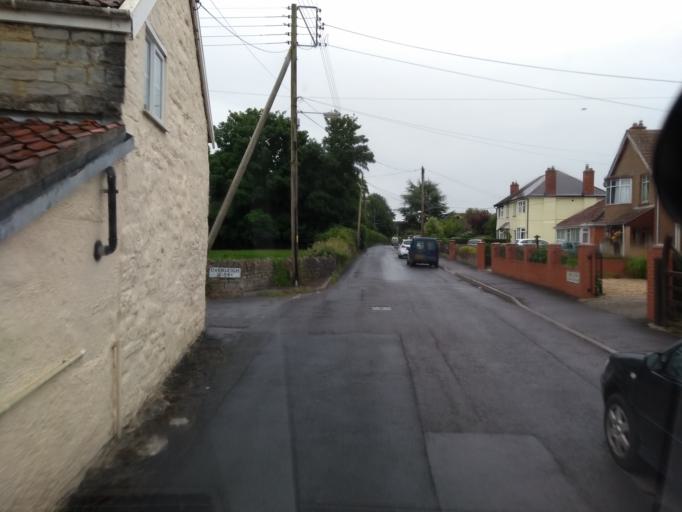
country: GB
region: England
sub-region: Somerset
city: Street
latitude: 51.1176
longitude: -2.7408
